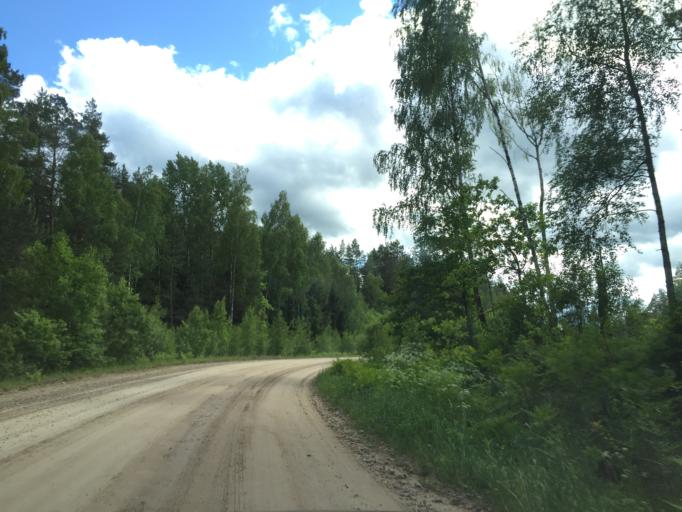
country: LV
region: Vecumnieki
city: Vecumnieki
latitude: 56.4925
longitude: 24.4092
